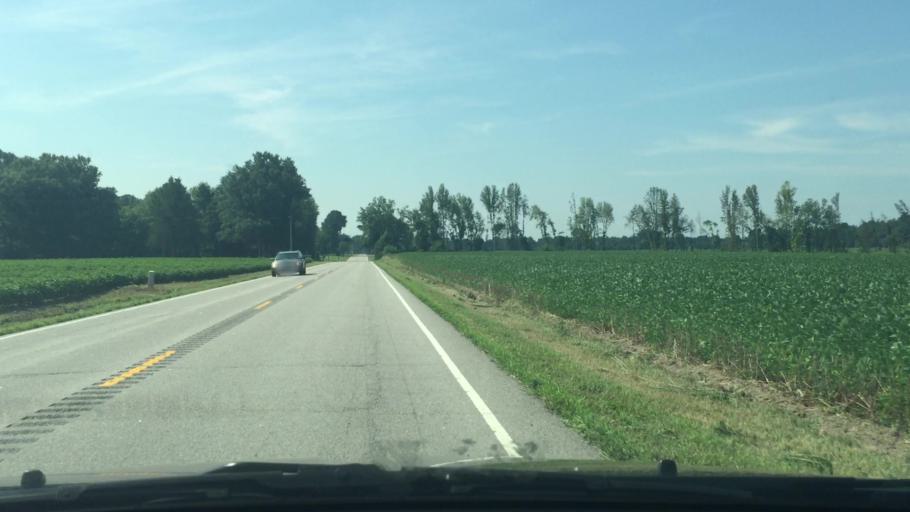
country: US
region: Virginia
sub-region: Southampton County
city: Courtland
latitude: 36.8002
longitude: -77.1287
